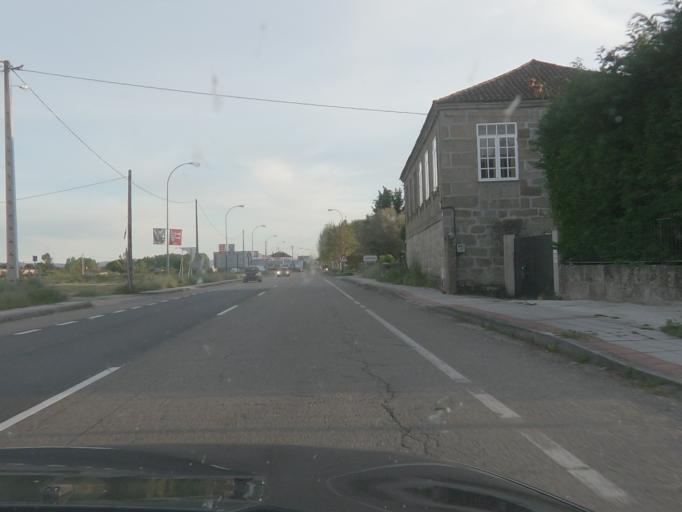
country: ES
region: Galicia
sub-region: Provincia de Ourense
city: Verin
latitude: 41.9286
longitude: -7.4412
